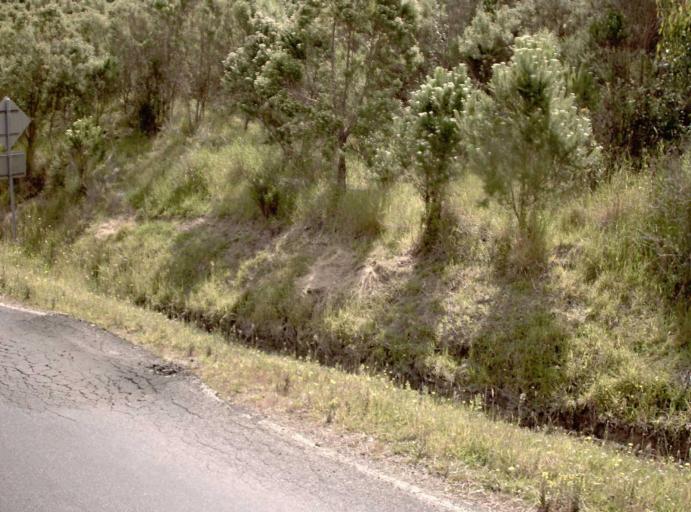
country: AU
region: Victoria
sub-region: Latrobe
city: Traralgon
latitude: -38.3694
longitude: 146.5672
